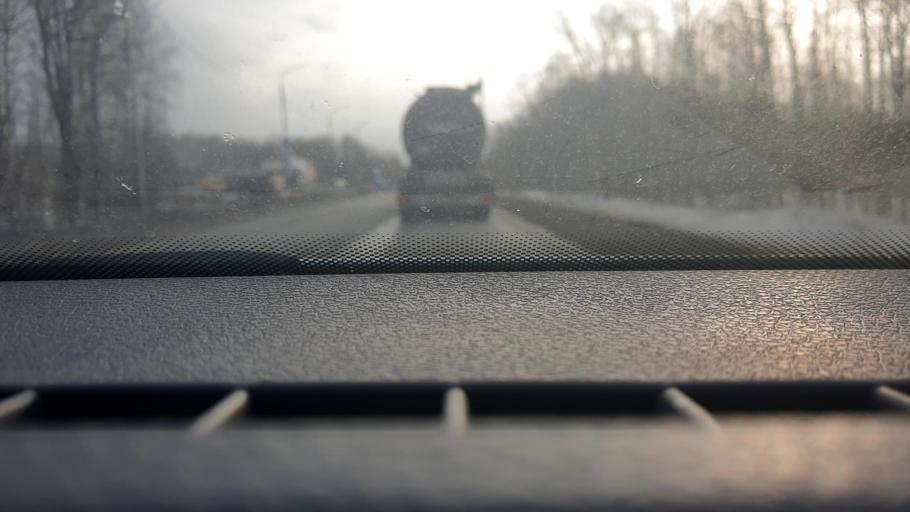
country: RU
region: Chelyabinsk
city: Asha
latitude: 54.8823
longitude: 57.2578
